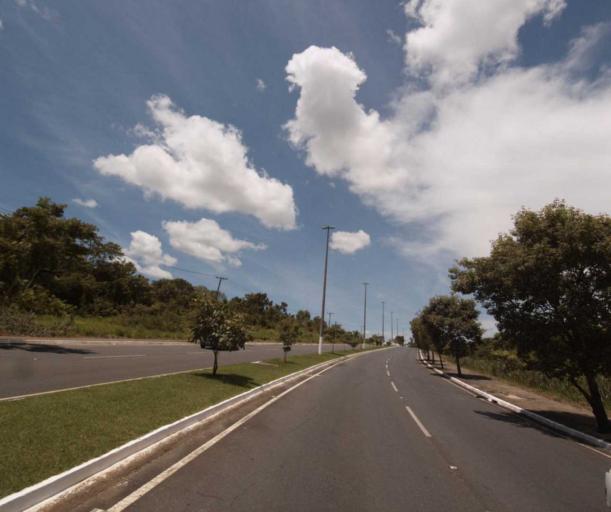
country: BR
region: Mato Grosso
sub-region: Cuiaba
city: Cuiaba
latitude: -15.5712
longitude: -56.1079
